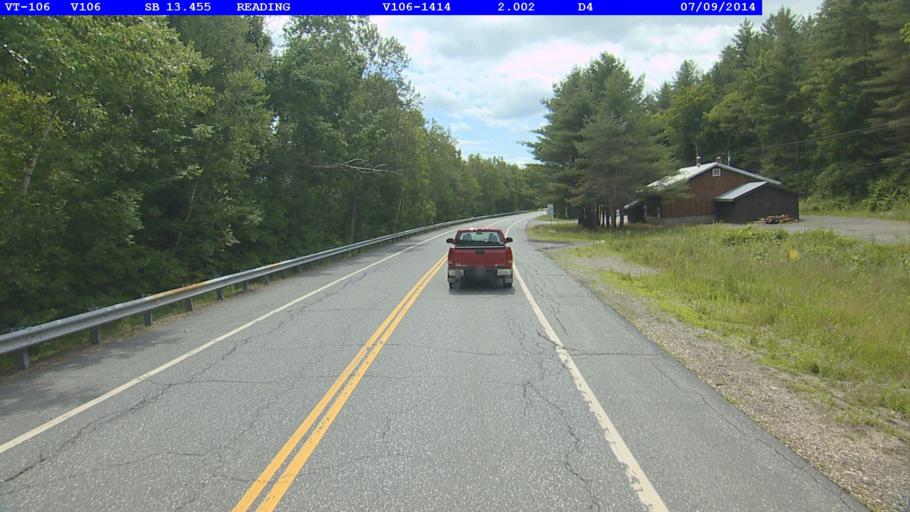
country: US
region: Vermont
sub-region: Windsor County
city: Windsor
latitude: 43.4721
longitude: -72.5348
